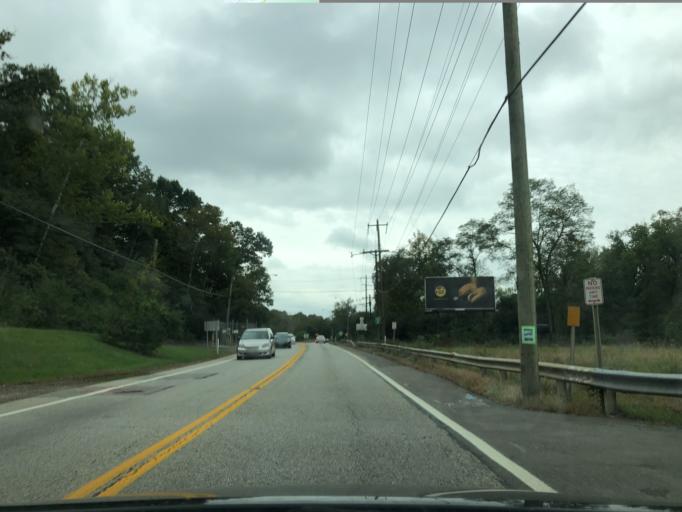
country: US
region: Ohio
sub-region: Hamilton County
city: Turpin Hills
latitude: 39.1105
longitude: -84.3989
